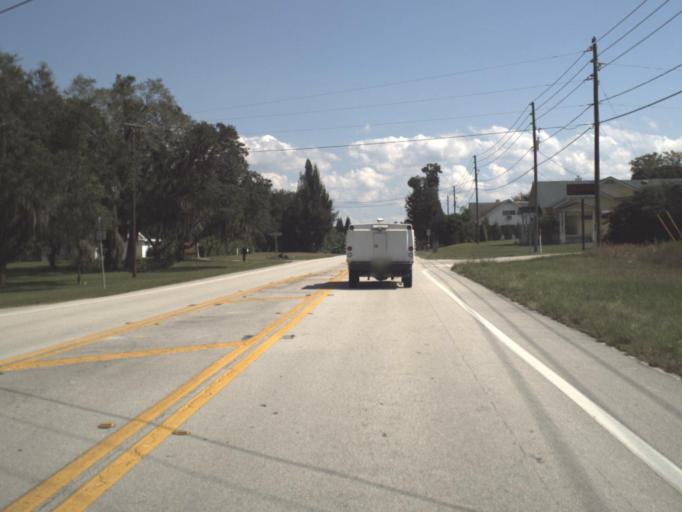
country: US
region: Florida
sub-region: Highlands County
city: Sebring
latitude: 27.4281
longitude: -81.4122
